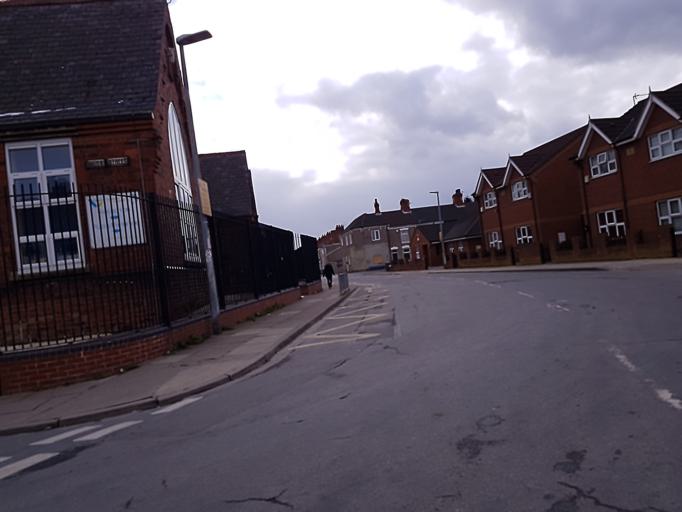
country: GB
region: England
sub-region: North East Lincolnshire
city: Grimsby
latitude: 53.5700
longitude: -0.0664
